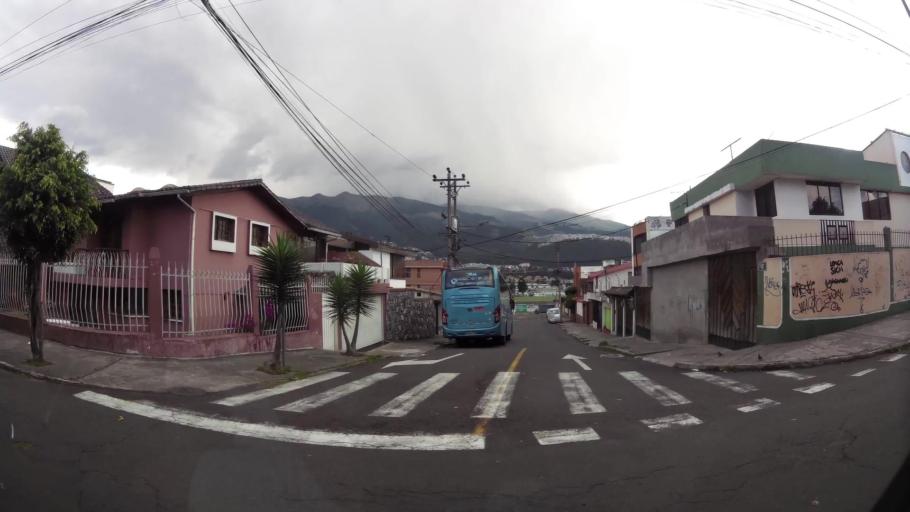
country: EC
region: Pichincha
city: Quito
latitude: -0.1332
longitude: -78.4870
